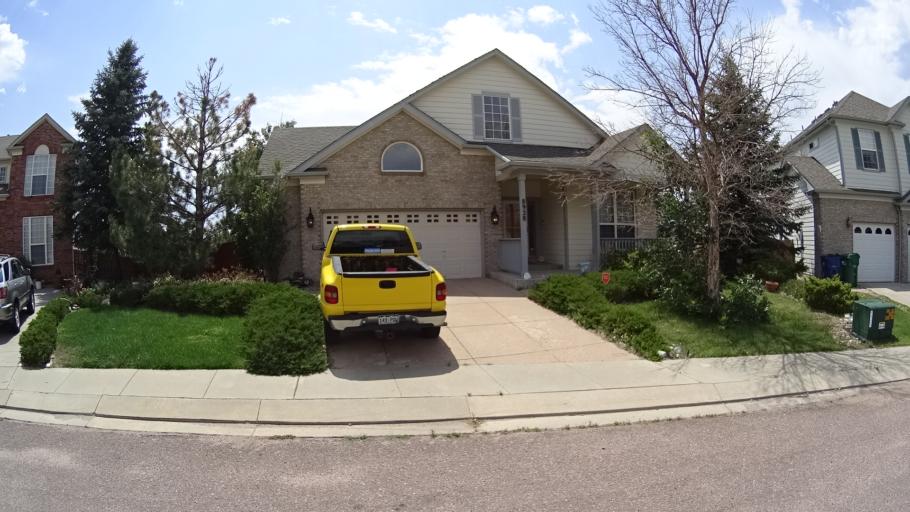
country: US
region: Colorado
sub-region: El Paso County
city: Black Forest
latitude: 38.9611
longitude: -104.7624
